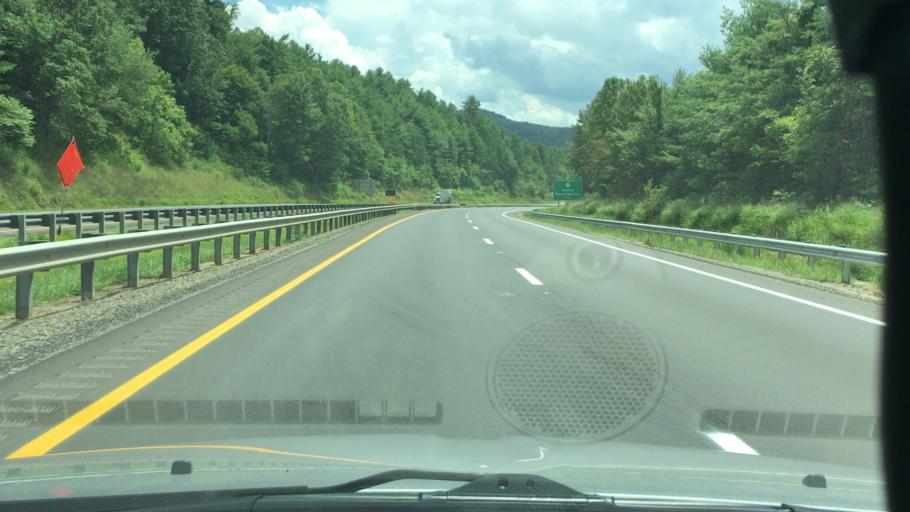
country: US
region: North Carolina
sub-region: Madison County
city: Mars Hill
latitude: 35.7766
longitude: -82.5390
